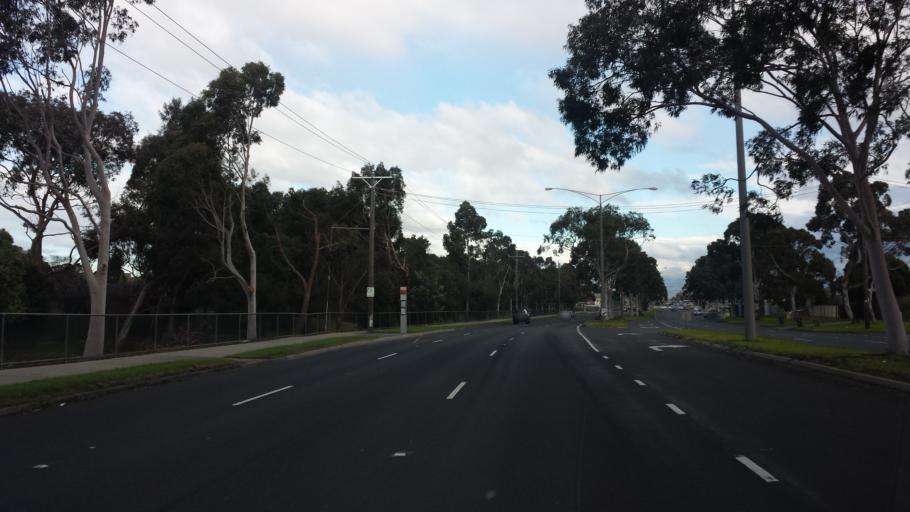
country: AU
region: Victoria
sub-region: Greater Dandenong
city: Springvale
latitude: -37.9287
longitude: 145.1567
